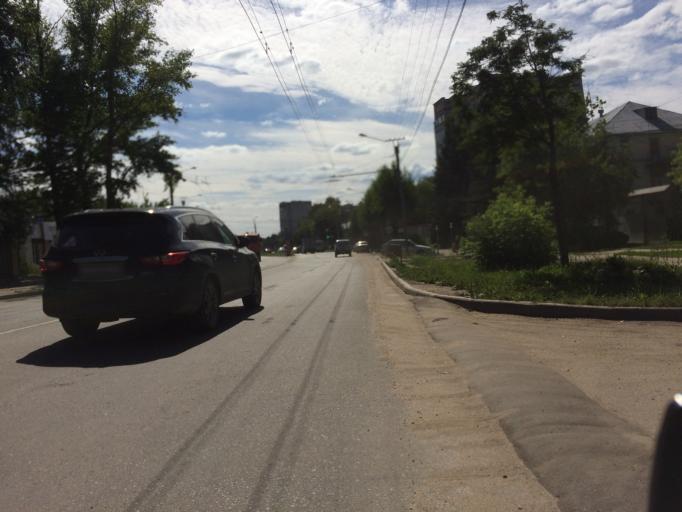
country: RU
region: Mariy-El
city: Yoshkar-Ola
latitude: 56.6358
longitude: 47.9440
